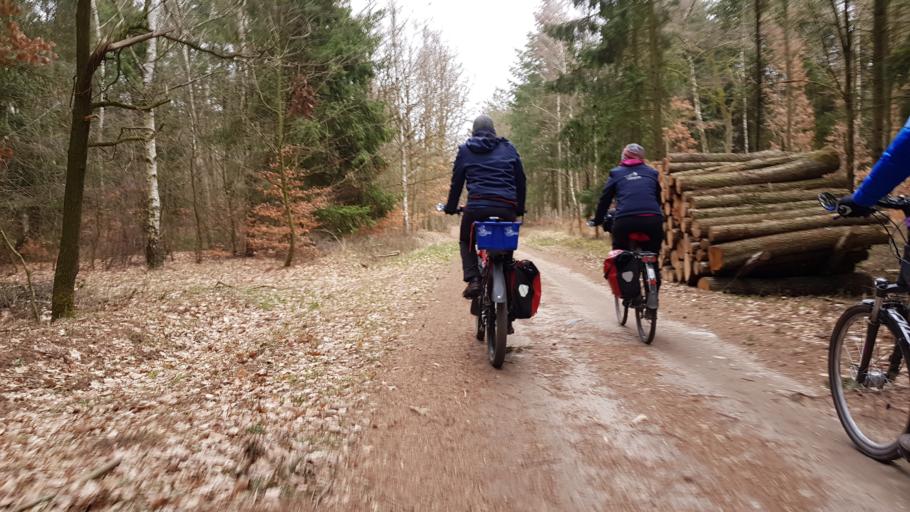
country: PL
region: West Pomeranian Voivodeship
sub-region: Powiat gryfinski
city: Banie
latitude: 53.0687
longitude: 14.7411
